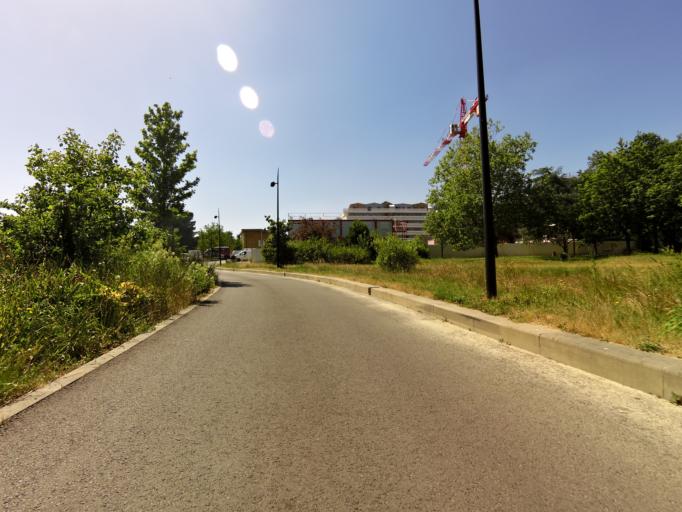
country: FR
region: Pays de la Loire
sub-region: Departement de la Loire-Atlantique
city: Saint-Herblain
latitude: 47.2175
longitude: -1.6163
